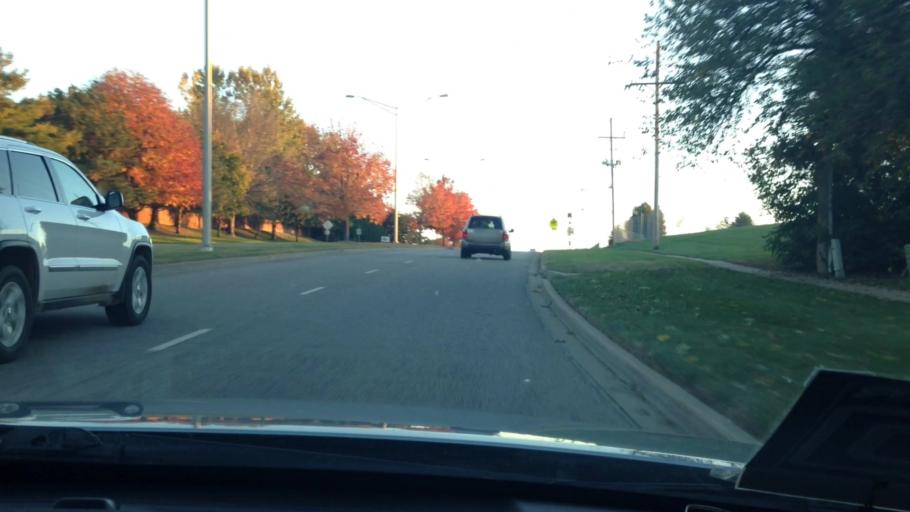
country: US
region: Kansas
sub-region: Johnson County
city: Lenexa
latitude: 38.8913
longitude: -94.7005
